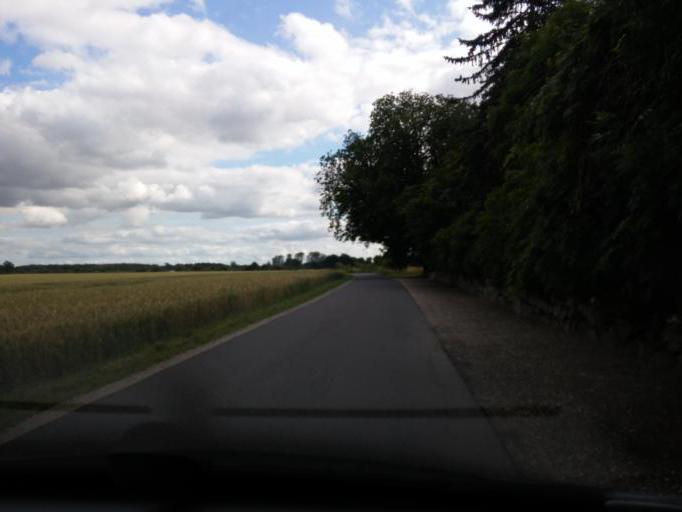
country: DK
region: South Denmark
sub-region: Kerteminde Kommune
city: Munkebo
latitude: 55.4149
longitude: 10.5586
